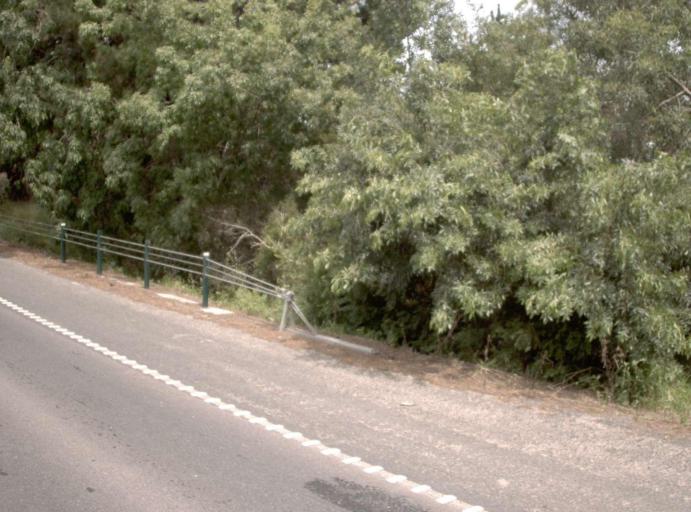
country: AU
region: Victoria
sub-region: Mornington Peninsula
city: Tyabb
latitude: -38.2624
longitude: 145.2028
